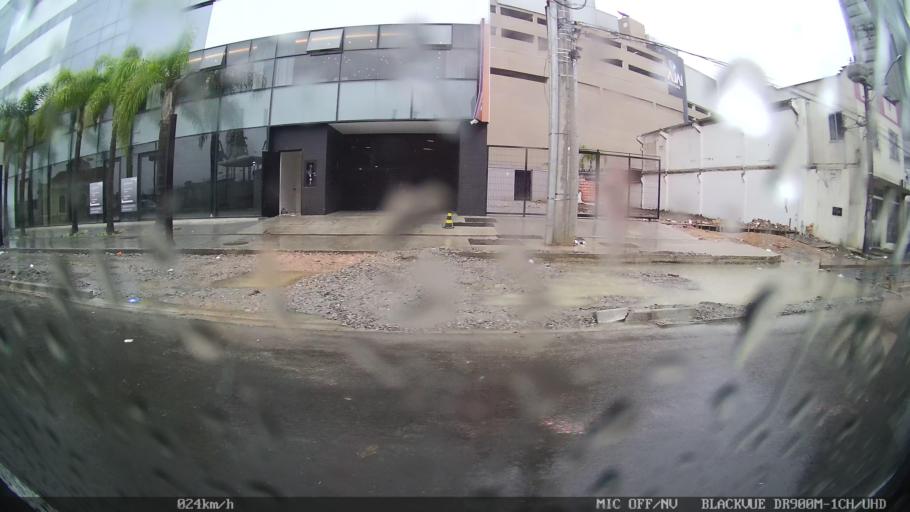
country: BR
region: Santa Catarina
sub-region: Itajai
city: Itajai
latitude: -26.9027
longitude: -48.6598
